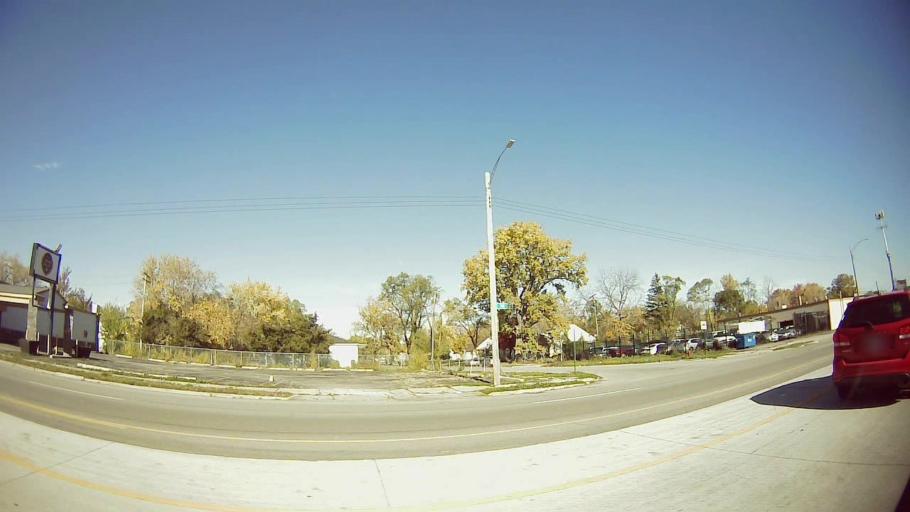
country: US
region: Michigan
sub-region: Wayne County
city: Dearborn Heights
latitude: 42.3574
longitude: -83.2387
